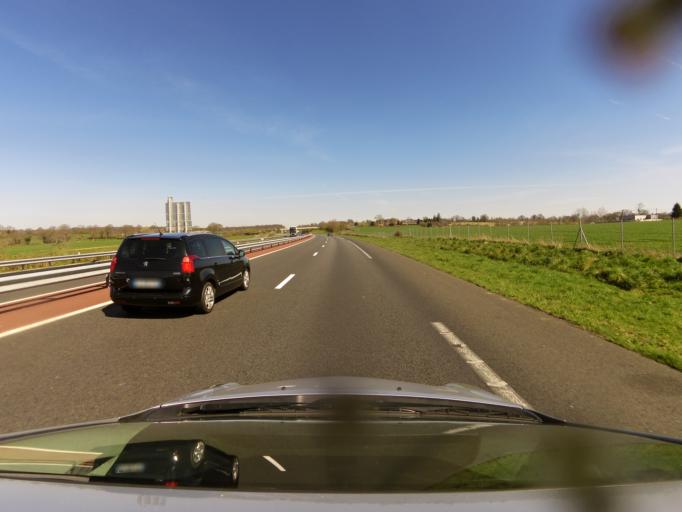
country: FR
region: Lower Normandy
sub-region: Departement de la Manche
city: Saint-Senier-sous-Avranches
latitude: 48.7507
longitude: -1.2795
